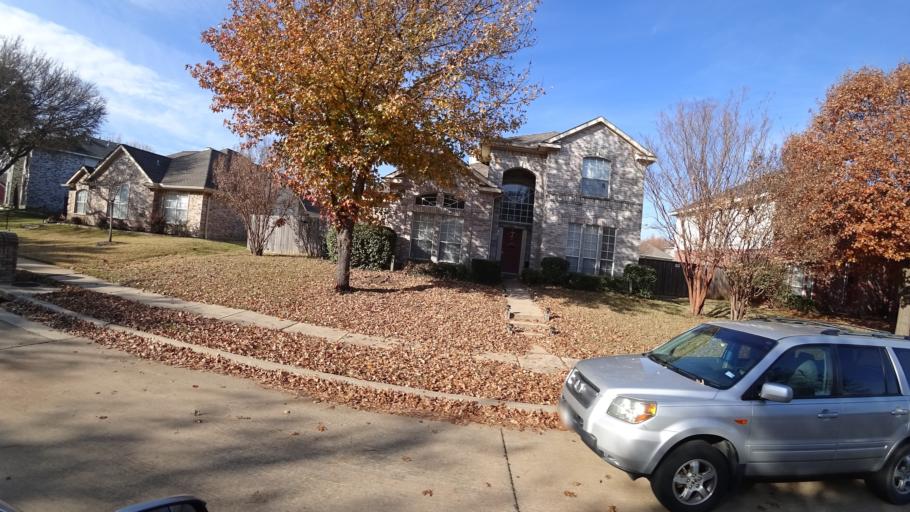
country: US
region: Texas
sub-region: Denton County
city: Lewisville
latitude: 33.0532
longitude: -97.0212
